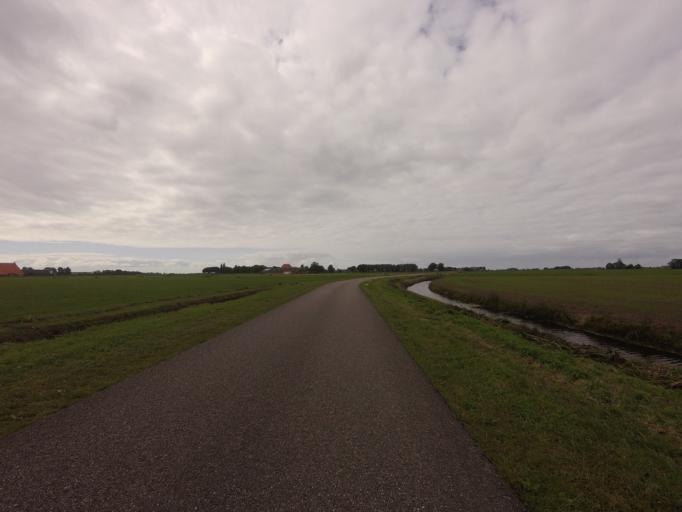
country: NL
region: Friesland
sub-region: Sudwest Fryslan
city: Koudum
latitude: 52.9481
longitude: 5.5105
